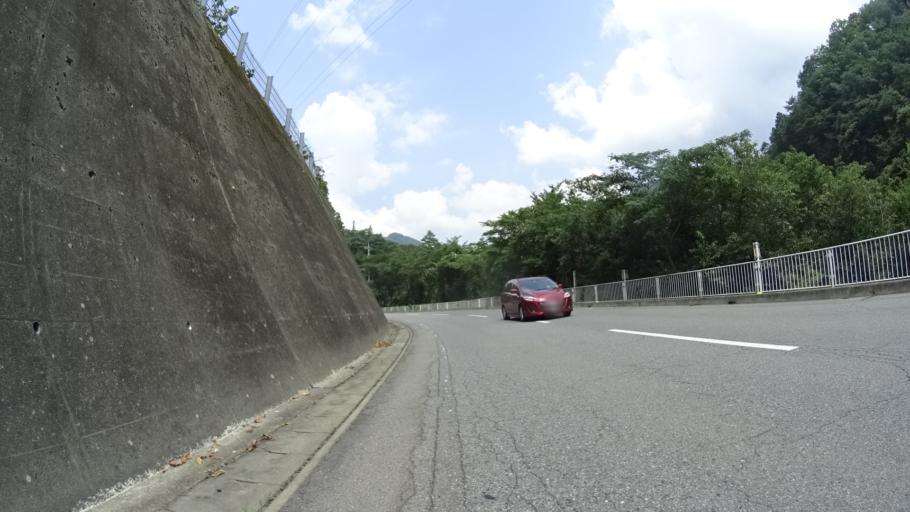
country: JP
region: Gunma
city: Tomioka
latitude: 36.0836
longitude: 138.7424
